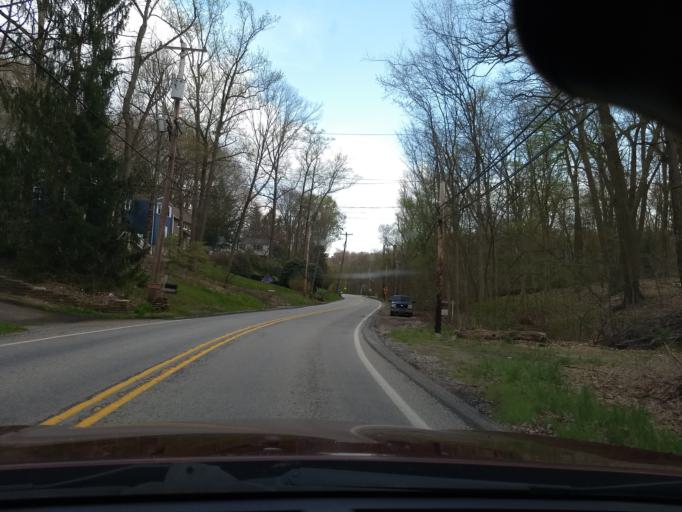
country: US
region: Pennsylvania
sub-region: Allegheny County
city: Fox Chapel
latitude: 40.5509
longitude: -79.8906
